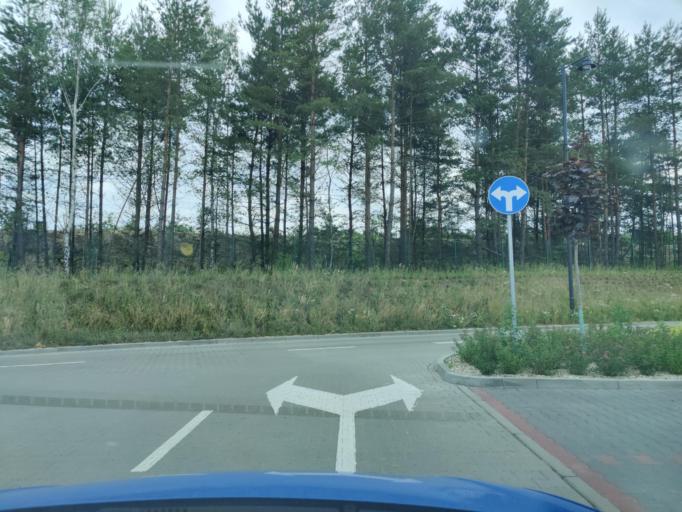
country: PL
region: Silesian Voivodeship
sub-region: Myslowice
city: Myslowice
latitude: 50.2297
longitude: 19.1743
